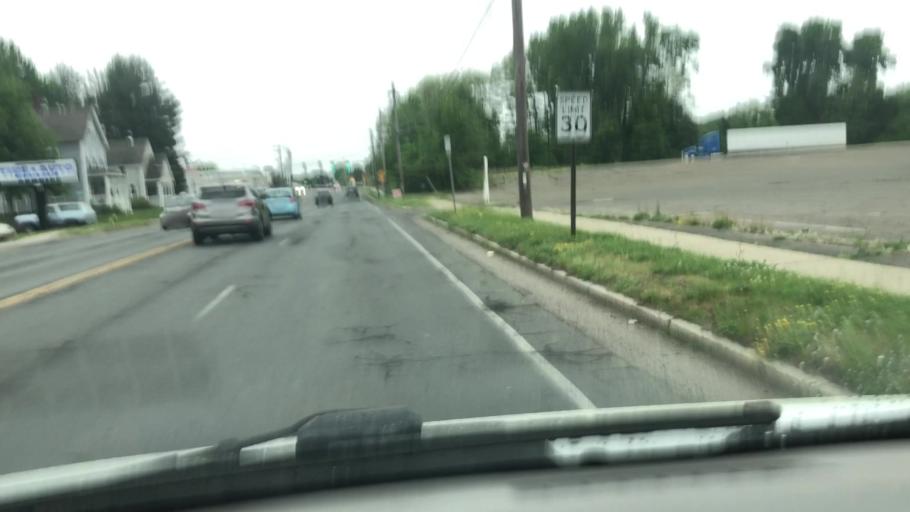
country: US
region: Massachusetts
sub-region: Hampshire County
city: Northampton
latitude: 42.3262
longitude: -72.6333
